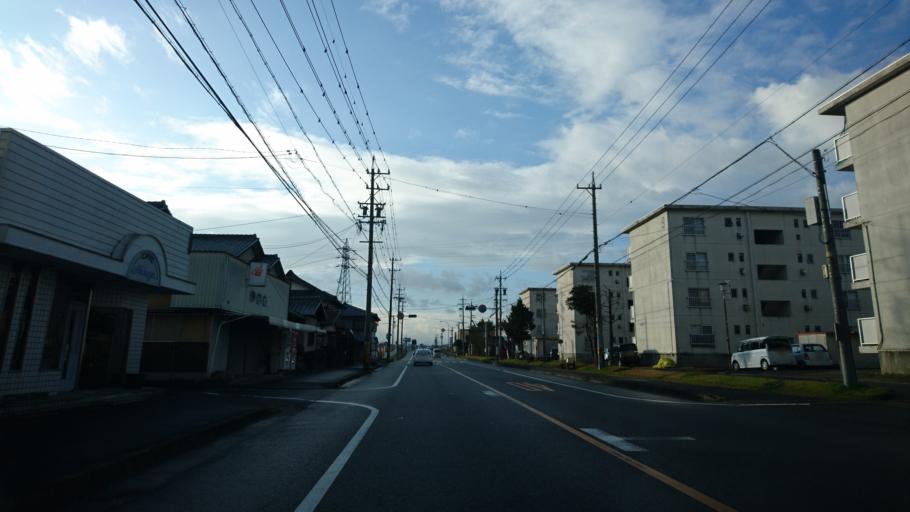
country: JP
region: Mie
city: Ueno-ebisumachi
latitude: 34.7541
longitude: 136.1230
